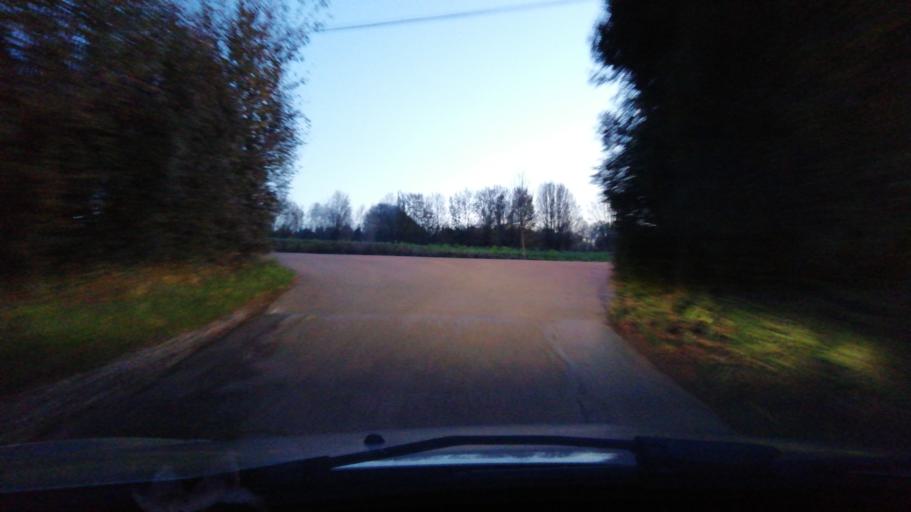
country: FR
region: Nord-Pas-de-Calais
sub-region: Departement du Nord
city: Marpent
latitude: 50.2522
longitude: 4.0926
